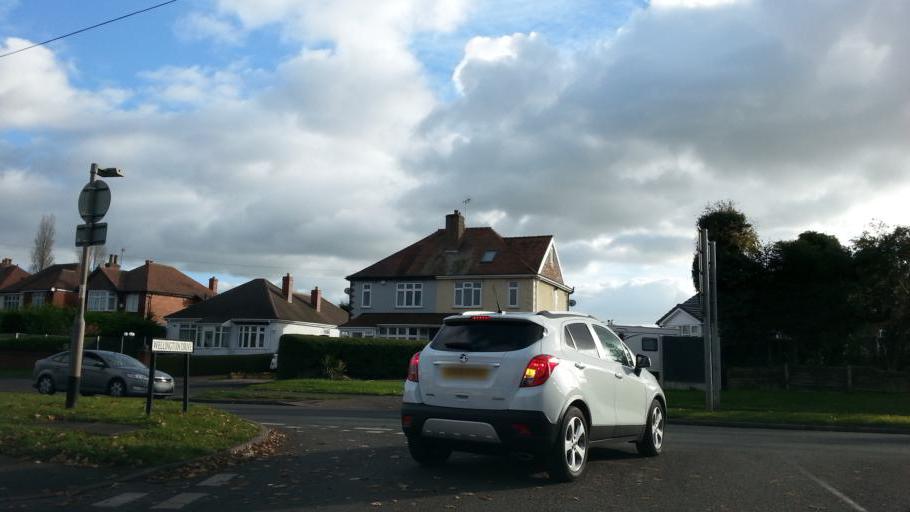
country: GB
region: England
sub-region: Staffordshire
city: Cannock
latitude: 52.6805
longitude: -2.0475
